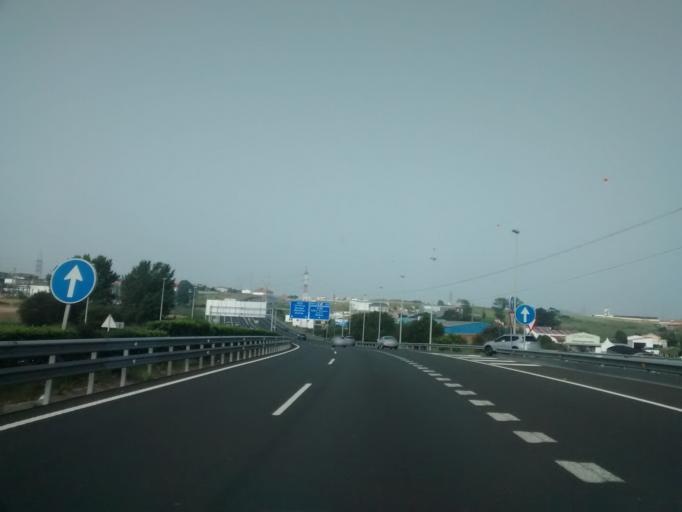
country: ES
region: Cantabria
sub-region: Provincia de Cantabria
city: Camargo
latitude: 43.4380
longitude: -3.8625
